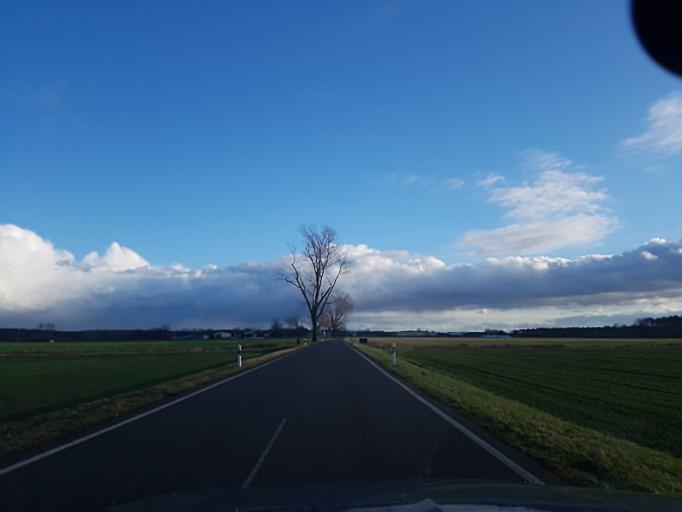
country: DE
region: Brandenburg
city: Schilda
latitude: 51.5581
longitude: 13.3500
